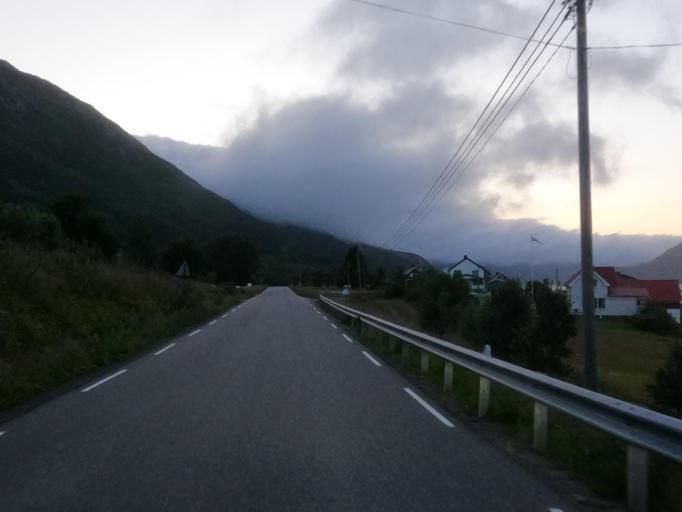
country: NO
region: Nordland
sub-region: Lodingen
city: Lodingen
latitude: 68.5679
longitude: 15.7990
